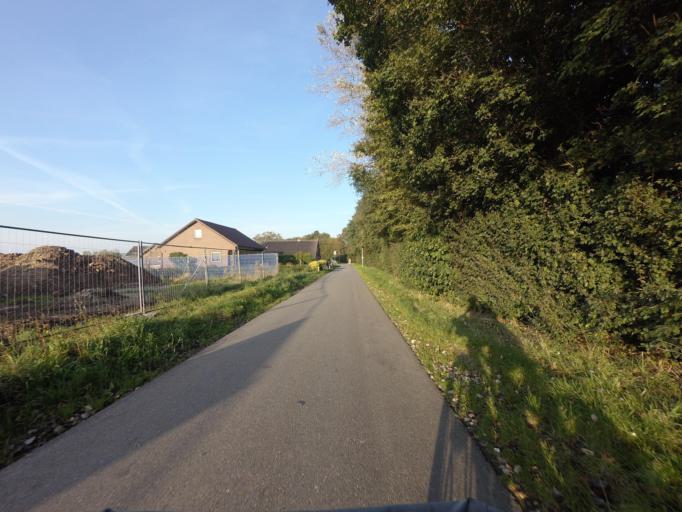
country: NL
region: Utrecht
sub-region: Gemeente Vianen
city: Vianen
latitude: 51.9870
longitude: 5.1255
